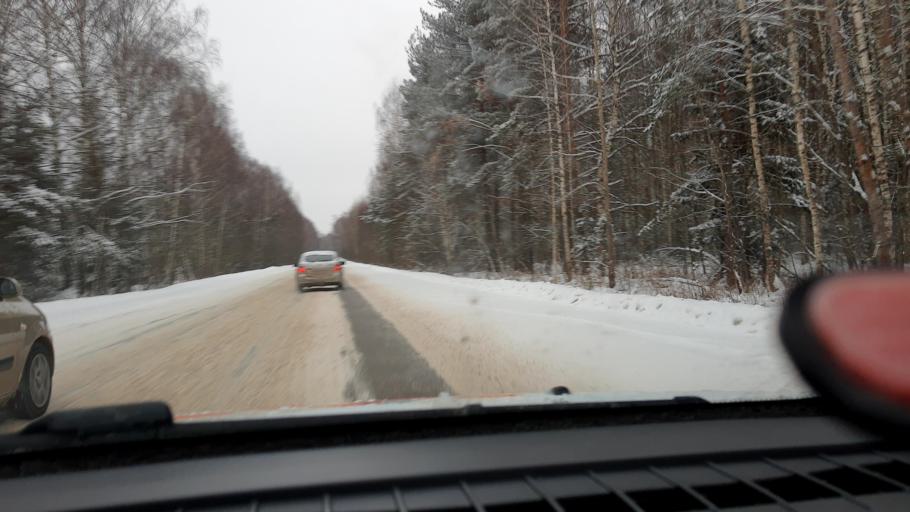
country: RU
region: Nizjnij Novgorod
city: Pamyat' Parizhskoy Kommuny
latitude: 56.2581
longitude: 44.4580
